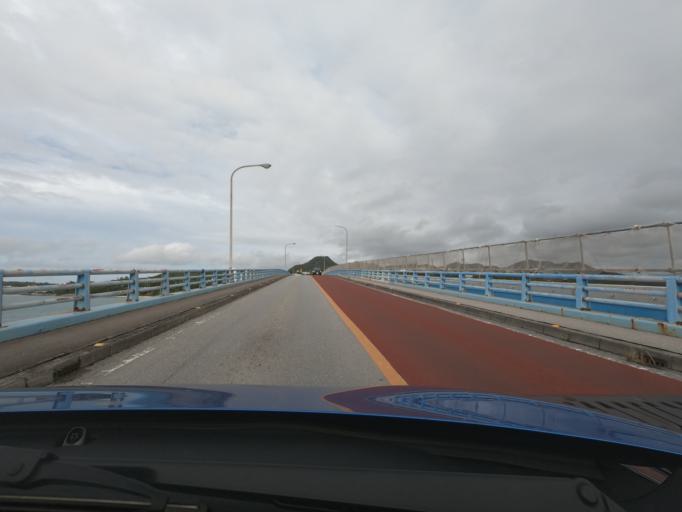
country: JP
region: Okinawa
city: Nago
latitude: 26.6599
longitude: 127.8882
